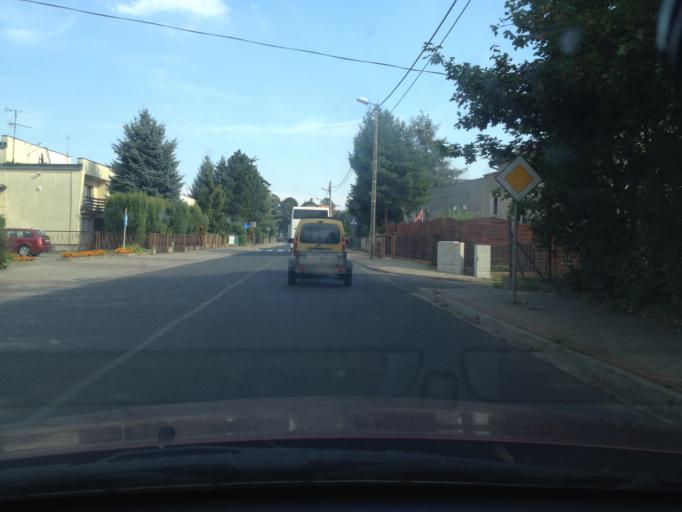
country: PL
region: Lower Silesian Voivodeship
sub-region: Powiat zgorzelecki
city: Zgorzelec
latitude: 51.1361
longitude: 15.0175
